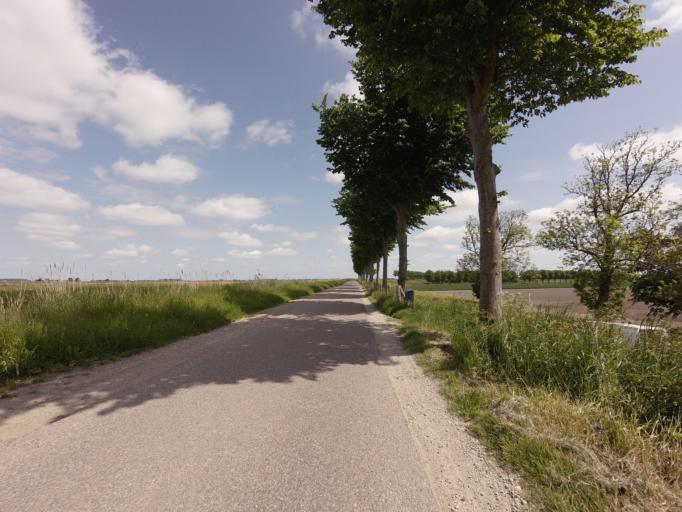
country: NL
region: North Holland
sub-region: Gemeente Beemster
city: Halfweg
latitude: 52.5745
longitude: 4.8670
